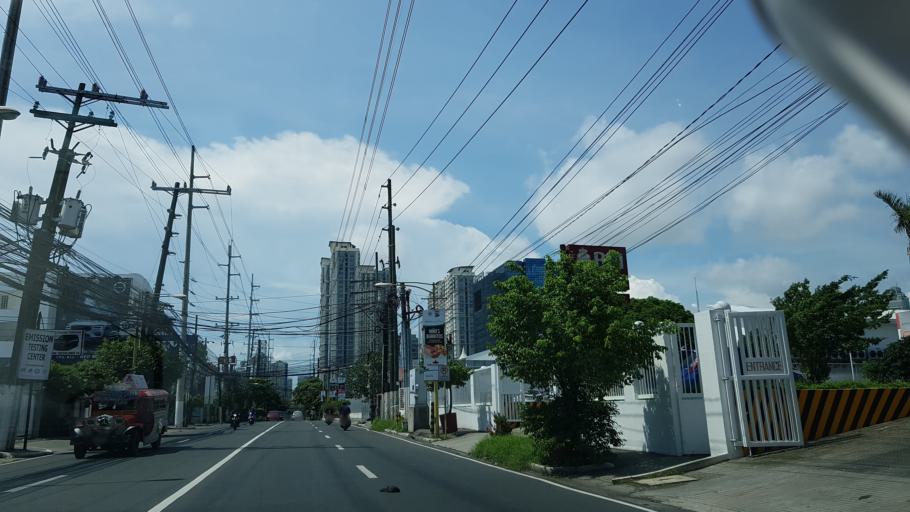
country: PH
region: Metro Manila
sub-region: Makati City
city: Makati City
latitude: 14.5379
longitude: 121.0202
